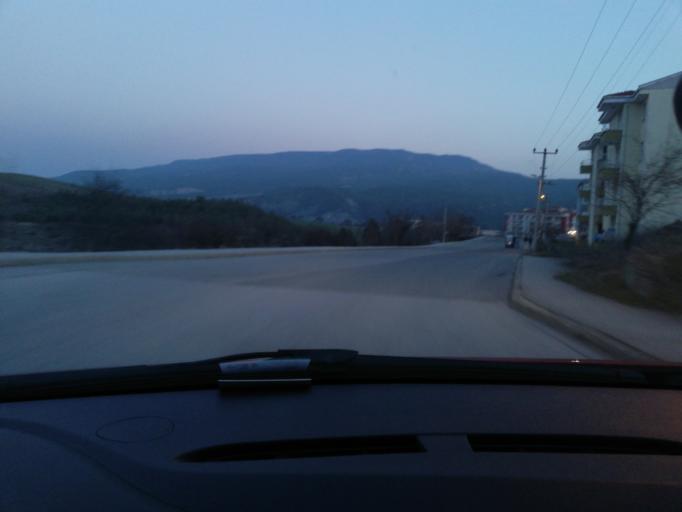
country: TR
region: Karabuk
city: Safranbolu
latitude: 41.2242
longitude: 32.6719
